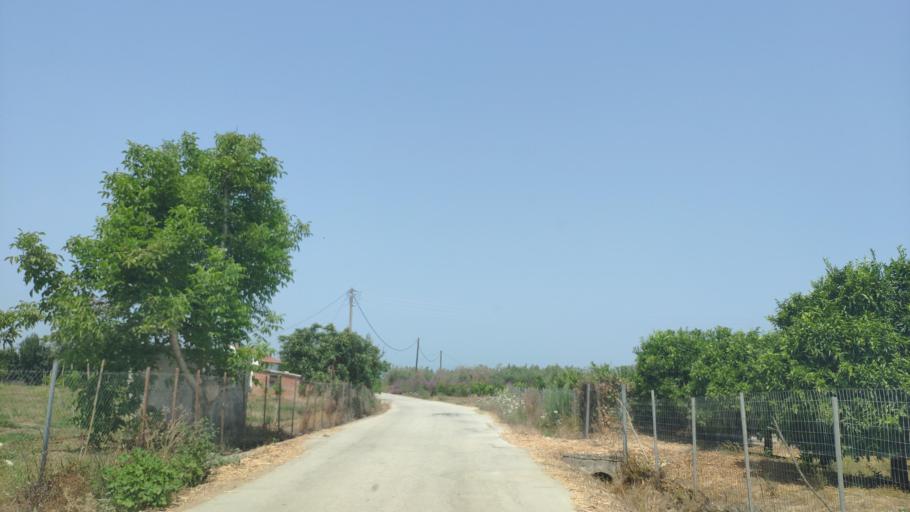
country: GR
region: Epirus
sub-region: Nomos Artas
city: Kompoti
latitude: 39.0590
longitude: 21.0665
